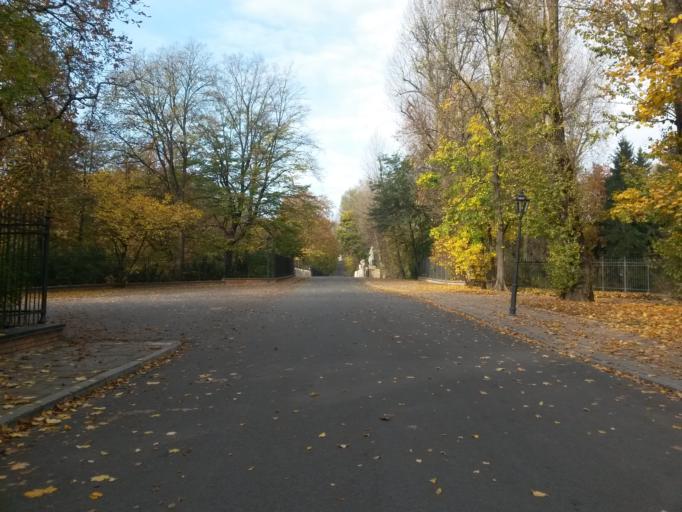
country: PL
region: Masovian Voivodeship
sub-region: Warszawa
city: Srodmiescie
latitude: 52.2172
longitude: 21.0367
